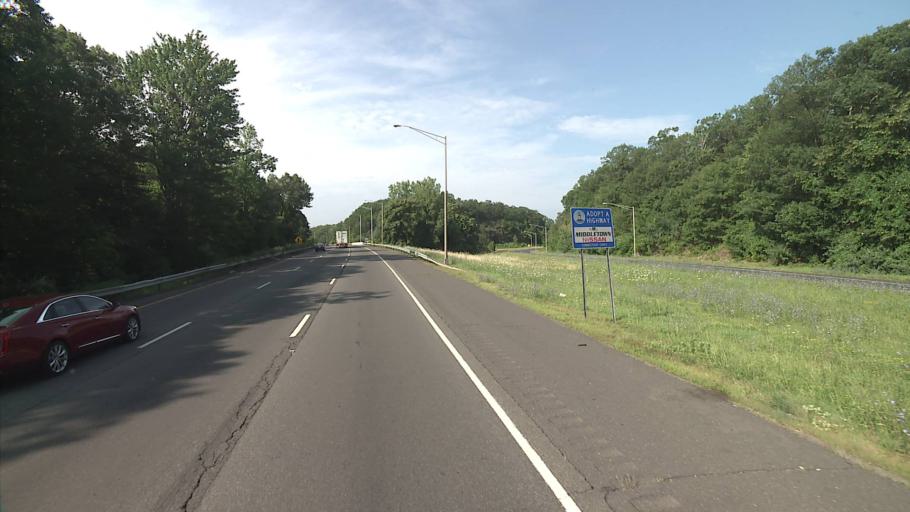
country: US
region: Connecticut
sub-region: Middlesex County
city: Cromwell
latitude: 41.6282
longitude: -72.6917
